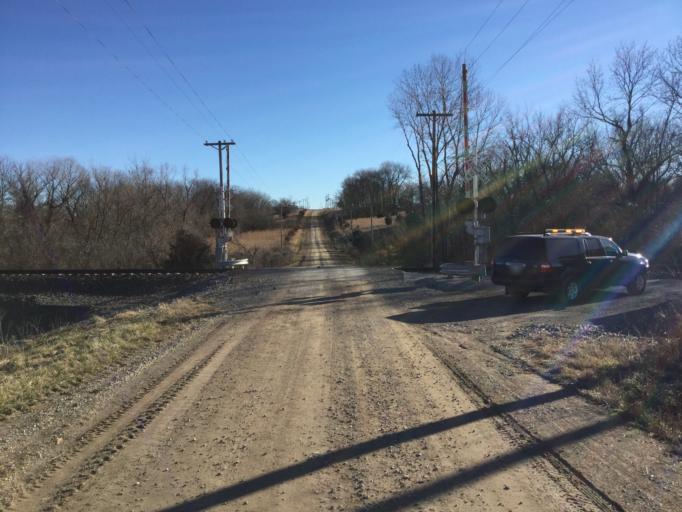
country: US
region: Kansas
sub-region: Miami County
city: Osawatomie
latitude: 38.3166
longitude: -94.9983
